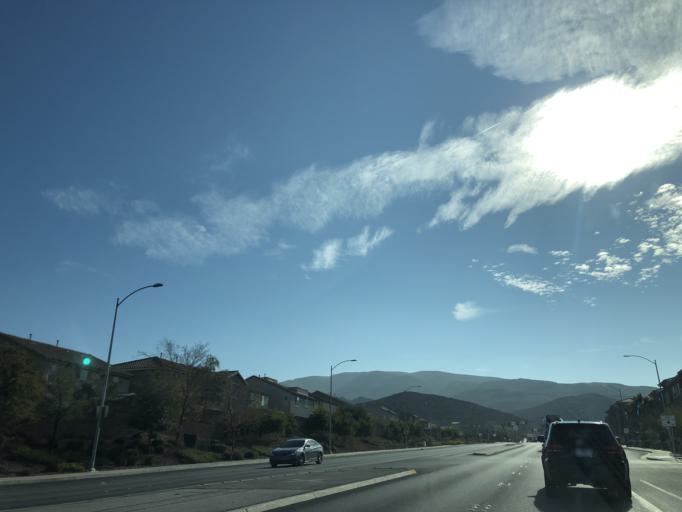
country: US
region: Nevada
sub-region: Clark County
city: Henderson
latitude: 36.0243
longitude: -115.0297
